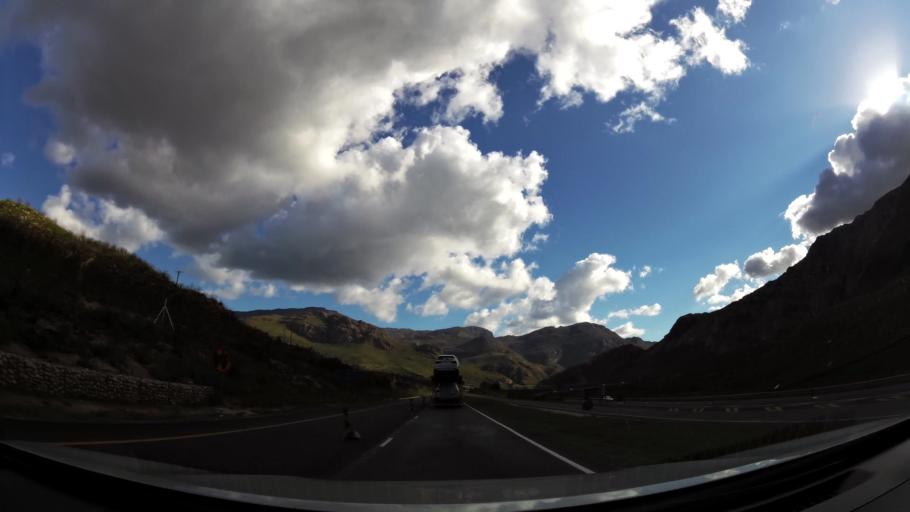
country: ZA
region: Western Cape
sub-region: Cape Winelands District Municipality
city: Paarl
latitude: -33.7261
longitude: 19.1415
